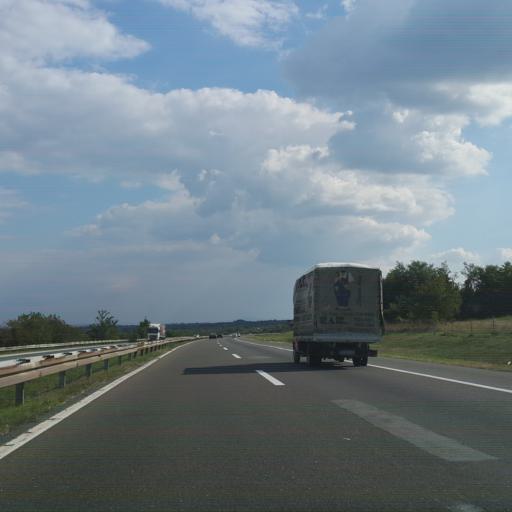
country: RS
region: Central Serbia
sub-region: Podunavski Okrug
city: Velika Plana
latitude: 44.4066
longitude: 21.0591
